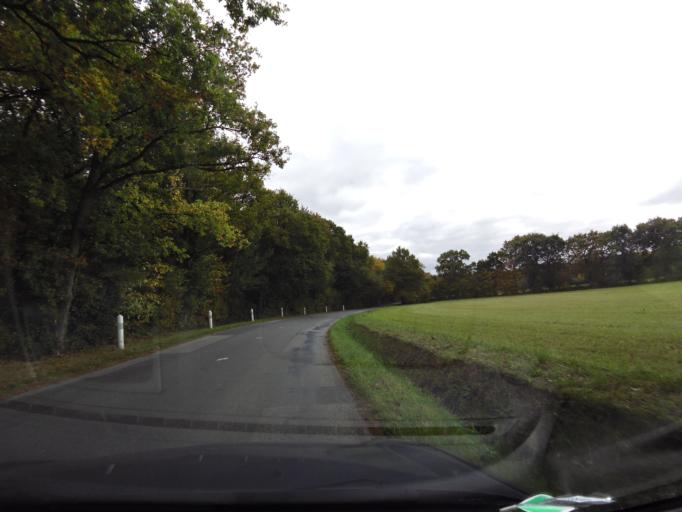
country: FR
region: Brittany
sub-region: Departement d'Ille-et-Vilaine
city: Chantepie
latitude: 48.0755
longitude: -1.6055
